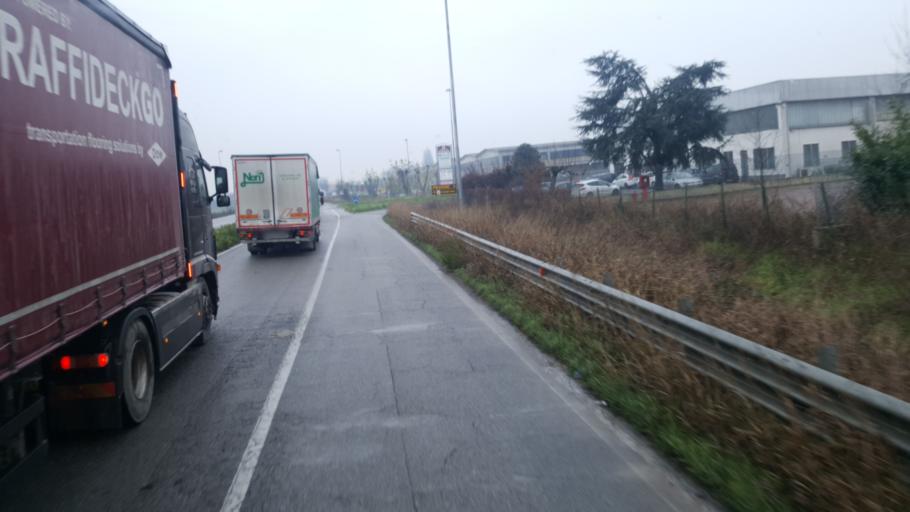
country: IT
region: Lombardy
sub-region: Provincia di Pavia
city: Siziano
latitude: 45.3259
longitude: 9.2164
